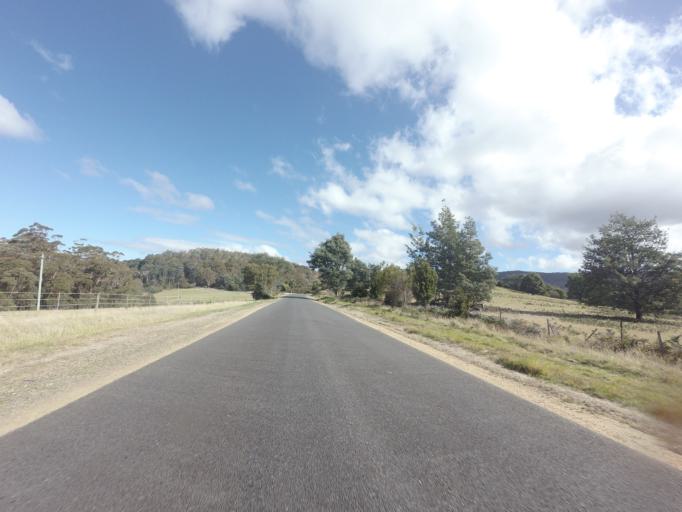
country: AU
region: Tasmania
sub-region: Break O'Day
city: St Helens
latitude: -41.6453
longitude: 148.2426
